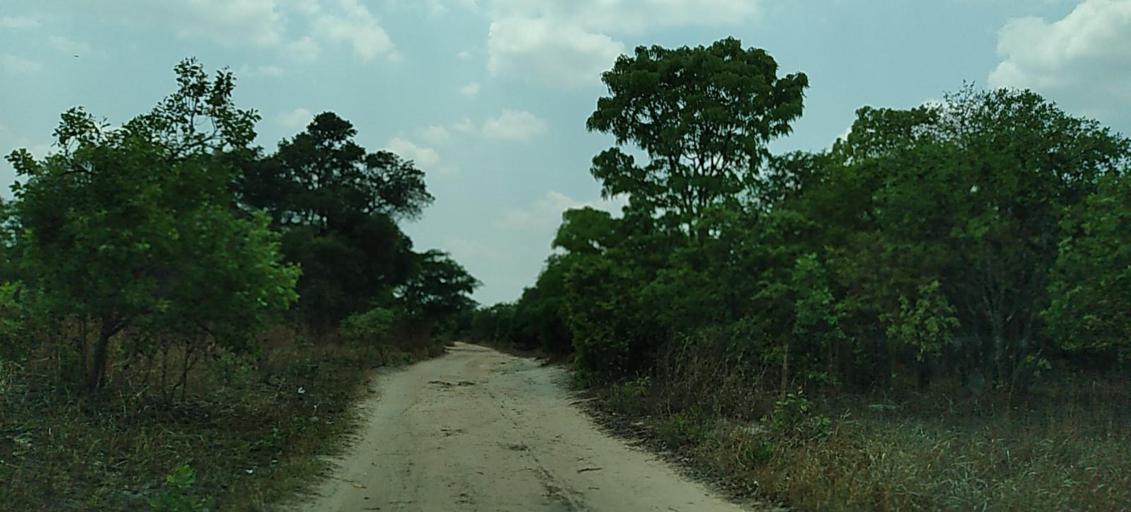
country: ZM
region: Copperbelt
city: Luanshya
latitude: -13.0990
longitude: 28.2970
